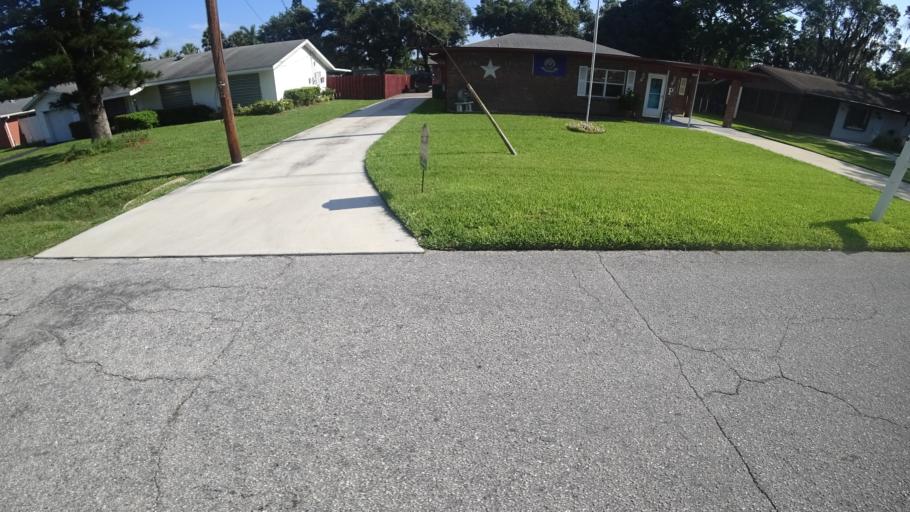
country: US
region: Florida
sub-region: Manatee County
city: South Bradenton
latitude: 27.4656
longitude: -82.5714
